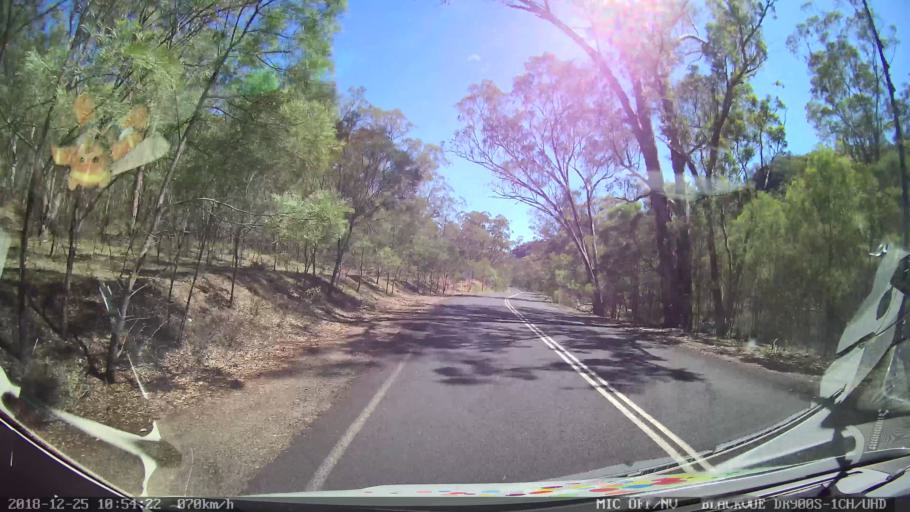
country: AU
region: New South Wales
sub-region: Upper Hunter Shire
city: Merriwa
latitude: -32.4105
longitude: 150.2730
